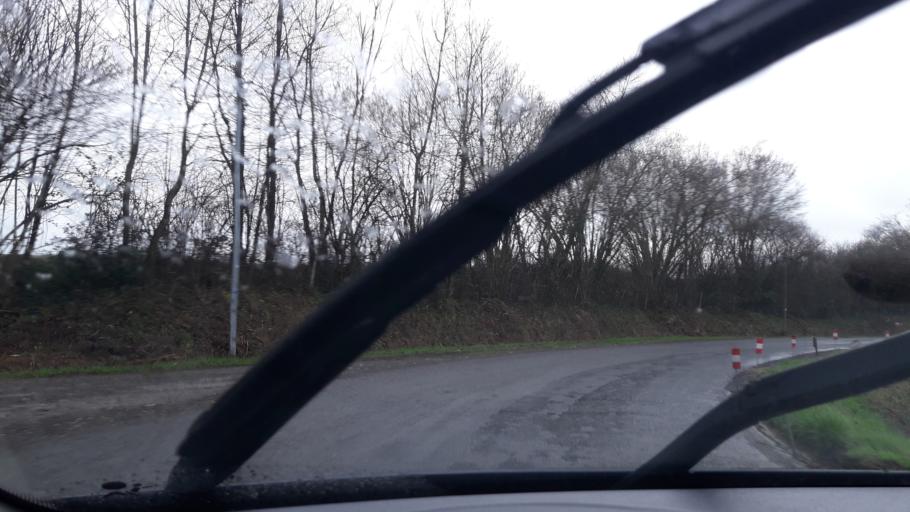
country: FR
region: Limousin
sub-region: Departement de la Haute-Vienne
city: Saint-Paul
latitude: 45.7676
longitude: 1.4311
